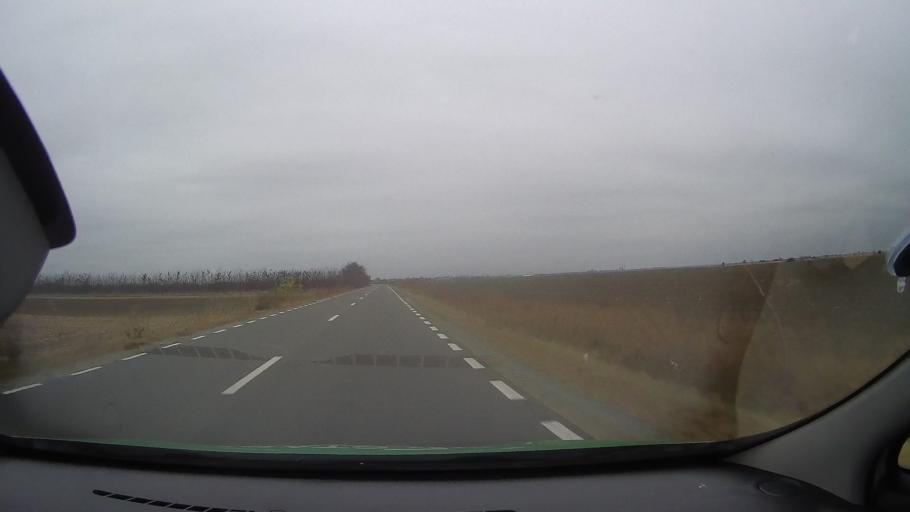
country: RO
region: Ialomita
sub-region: Comuna Slobozia
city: Slobozia
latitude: 44.6136
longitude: 27.3860
